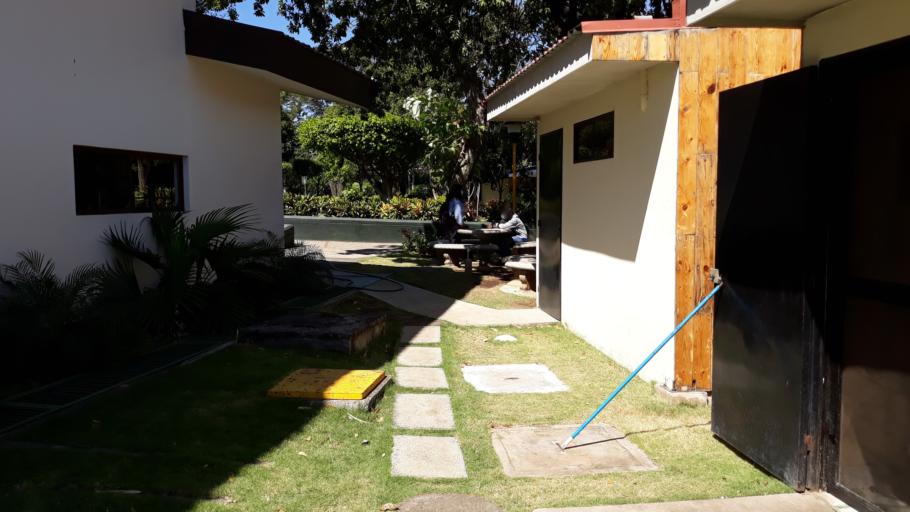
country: NI
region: Managua
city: Managua
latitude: 12.1250
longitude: -86.2720
